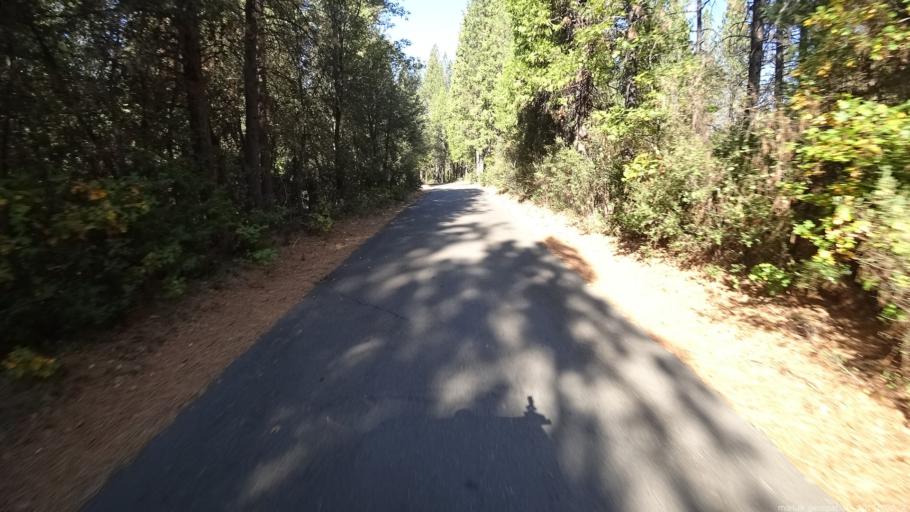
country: US
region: California
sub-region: Shasta County
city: Shingletown
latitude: 40.5315
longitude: -121.9295
